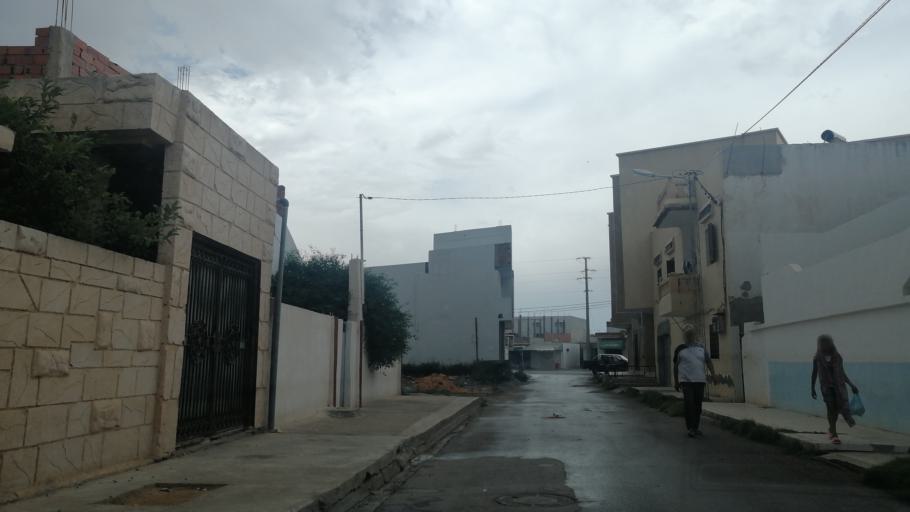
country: TN
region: Al Qayrawan
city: Sbikha
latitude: 36.1247
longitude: 10.0936
